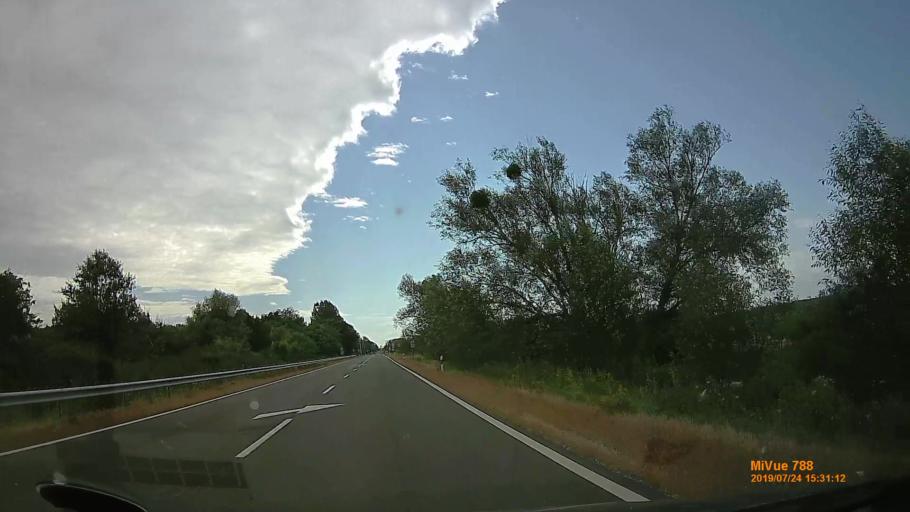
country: HU
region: Szabolcs-Szatmar-Bereg
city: Tarpa
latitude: 48.1559
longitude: 22.4360
